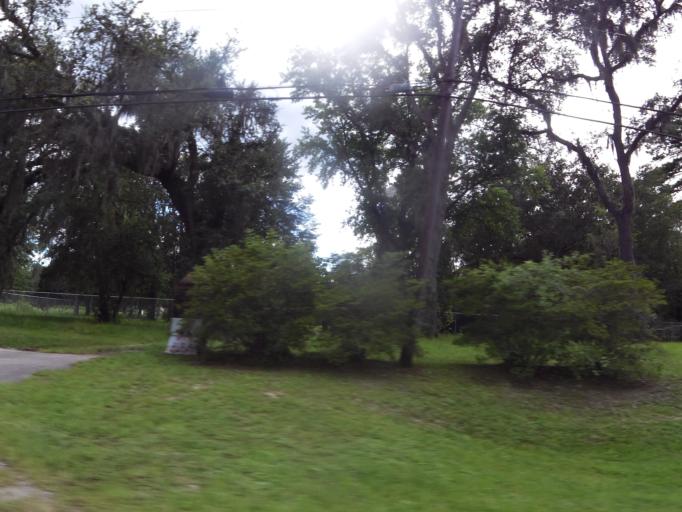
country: US
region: Florida
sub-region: Clay County
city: Asbury Lake
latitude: 30.0730
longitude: -81.7754
